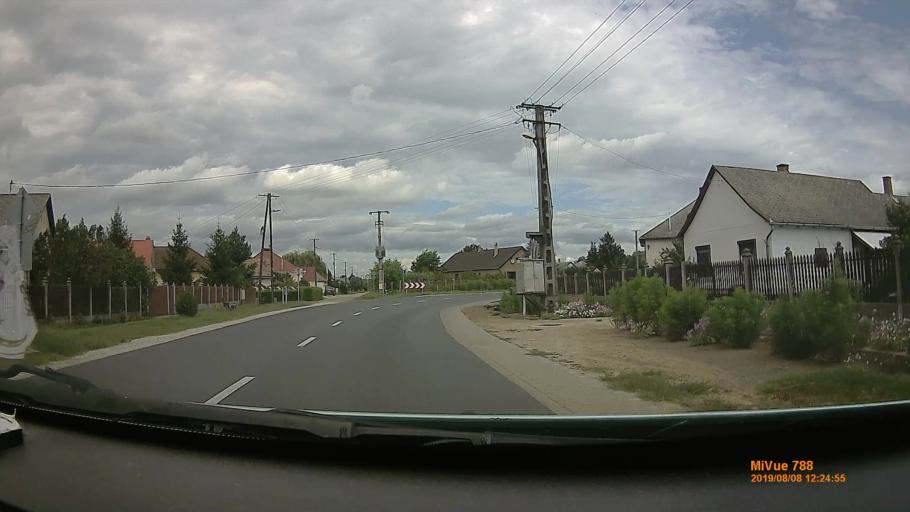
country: HU
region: Szabolcs-Szatmar-Bereg
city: Nyirbogat
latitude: 47.8080
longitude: 22.0661
